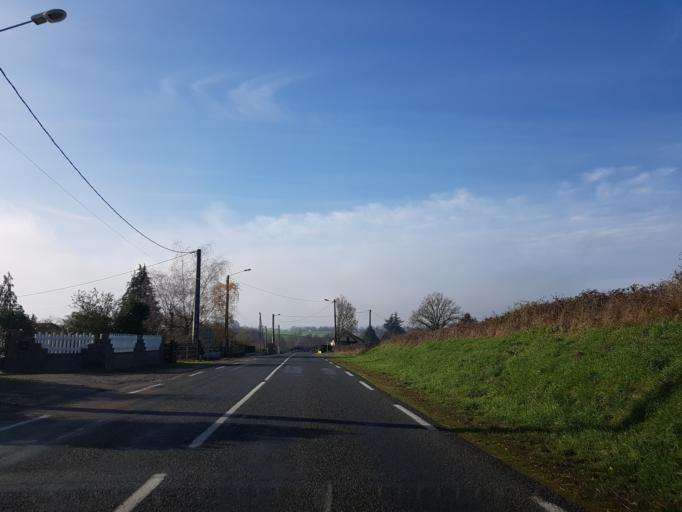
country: FR
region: Bourgogne
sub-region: Departement de Saone-et-Loire
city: Gueugnon
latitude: 46.5957
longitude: 4.0353
